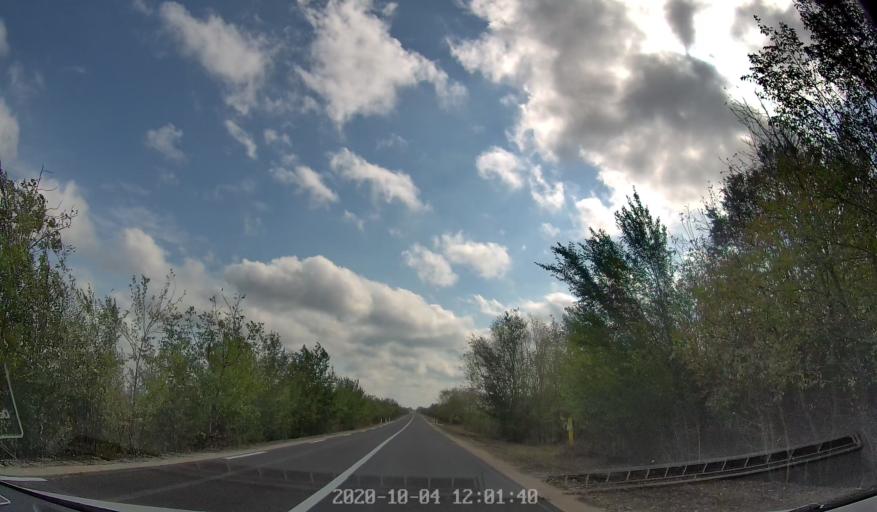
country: MD
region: Rezina
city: Saharna
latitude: 47.6231
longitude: 28.8926
